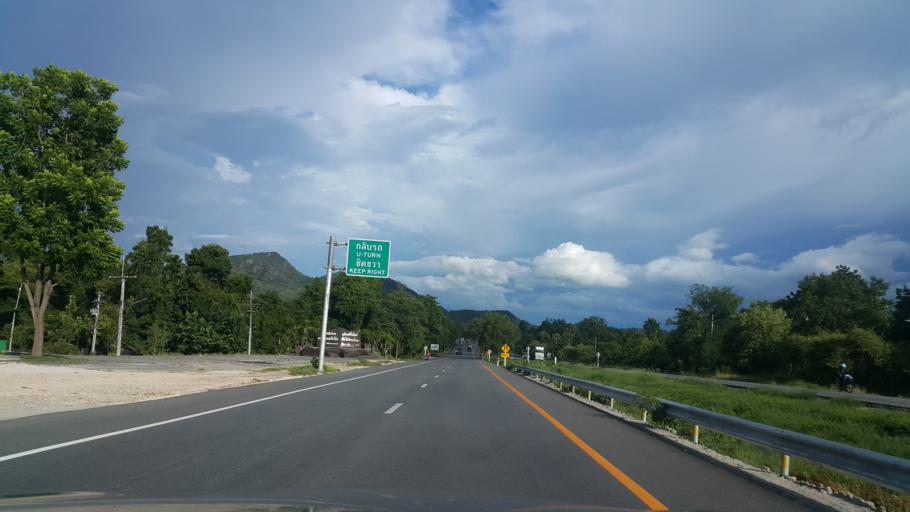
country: TH
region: Tak
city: Ban Tak
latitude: 17.0173
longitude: 99.1018
